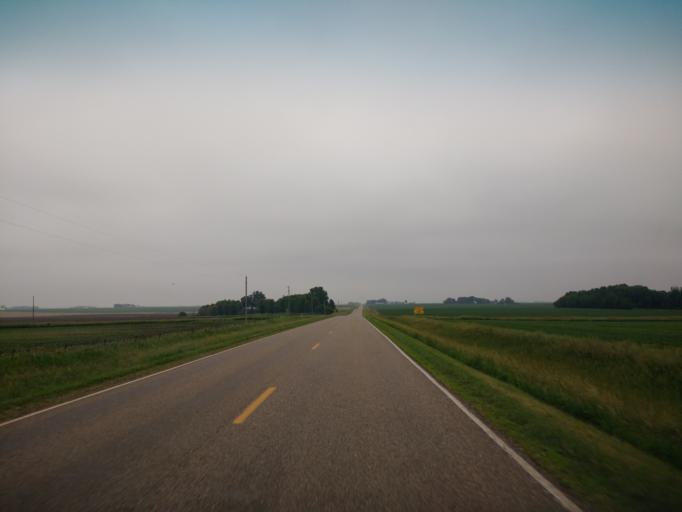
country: US
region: Iowa
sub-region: Sioux County
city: Alton
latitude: 42.9954
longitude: -95.8994
